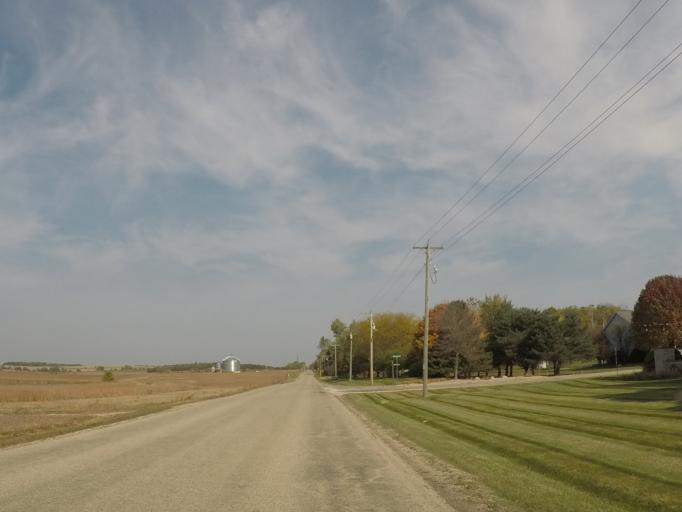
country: US
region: Wisconsin
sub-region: Dane County
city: Cross Plains
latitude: 43.0539
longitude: -89.6009
